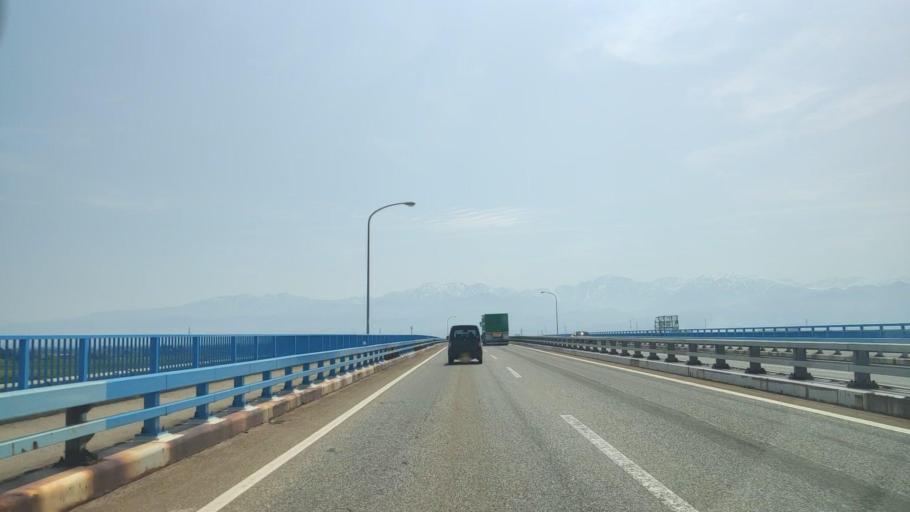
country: JP
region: Toyama
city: Toyama-shi
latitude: 36.7187
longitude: 137.2731
